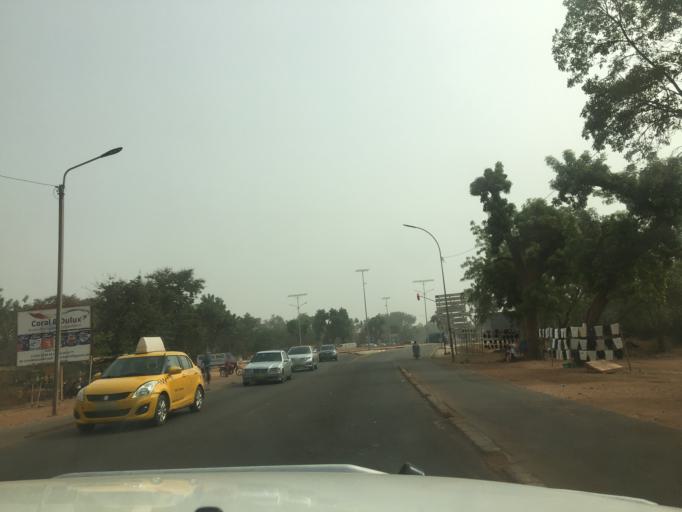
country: BF
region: Centre
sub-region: Kadiogo Province
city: Ouagadougou
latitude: 12.3956
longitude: -1.4987
